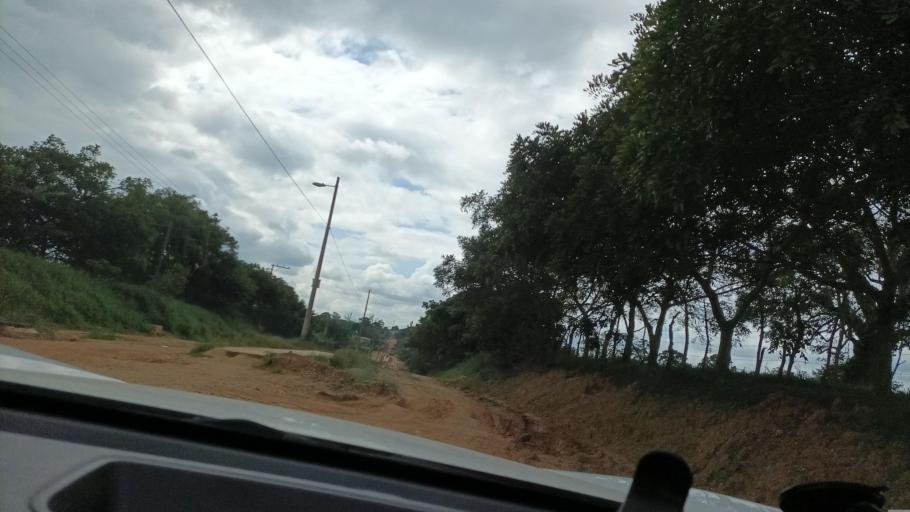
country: MX
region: Veracruz
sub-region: Soconusco
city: Fraccionamiento Santa Cruz
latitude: 17.9657
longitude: -94.8915
